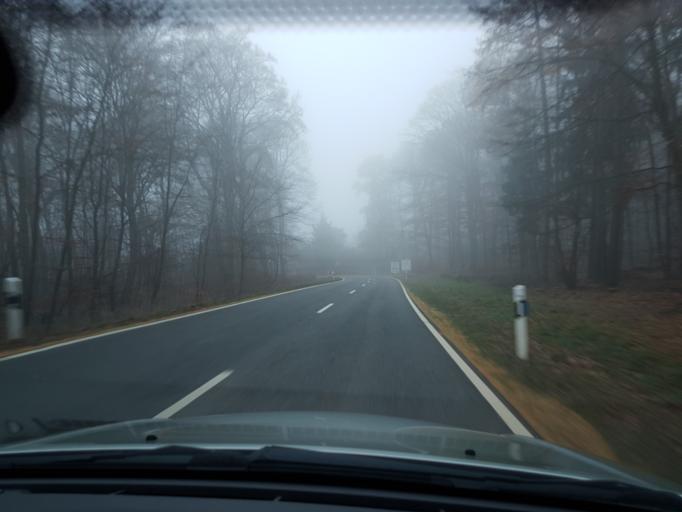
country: DE
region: Hesse
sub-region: Regierungsbezirk Darmstadt
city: Schlangenbad
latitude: 50.0799
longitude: 8.0459
